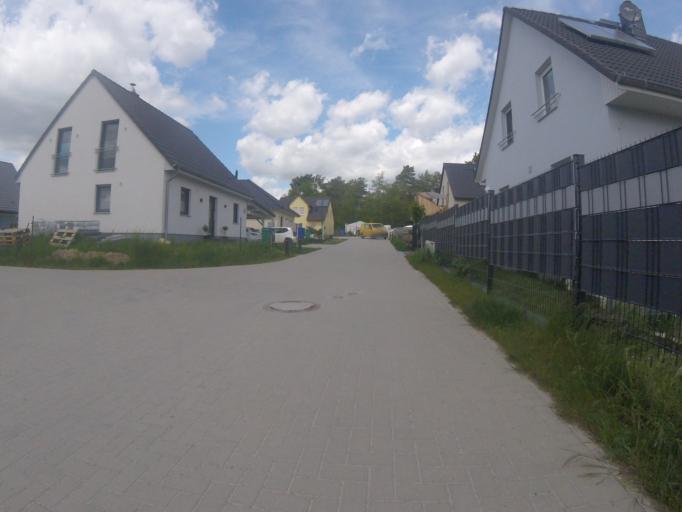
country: DE
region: Brandenburg
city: Bestensee
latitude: 52.2617
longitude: 13.6241
